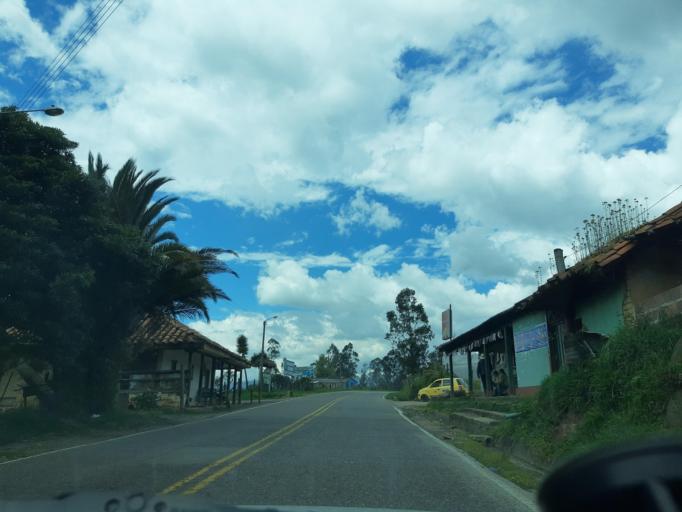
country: CO
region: Boyaca
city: Raquira
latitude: 5.5907
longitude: -73.7128
